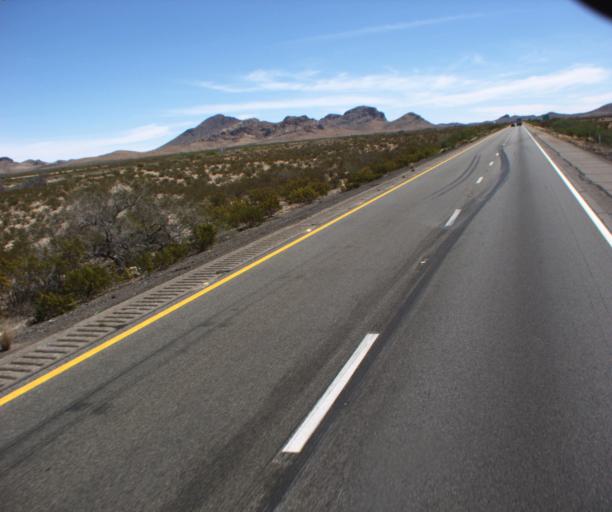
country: US
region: New Mexico
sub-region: Hidalgo County
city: Lordsburg
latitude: 32.2327
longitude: -109.0715
